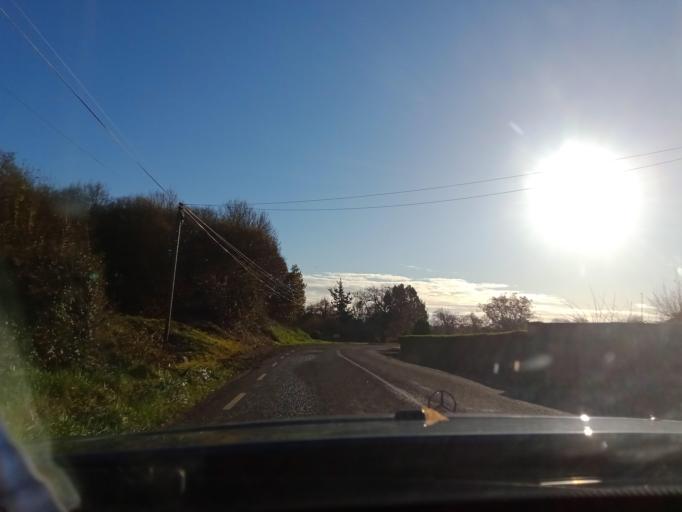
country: IE
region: Leinster
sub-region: Kilkenny
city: Piltown
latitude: 52.3904
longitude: -7.3482
